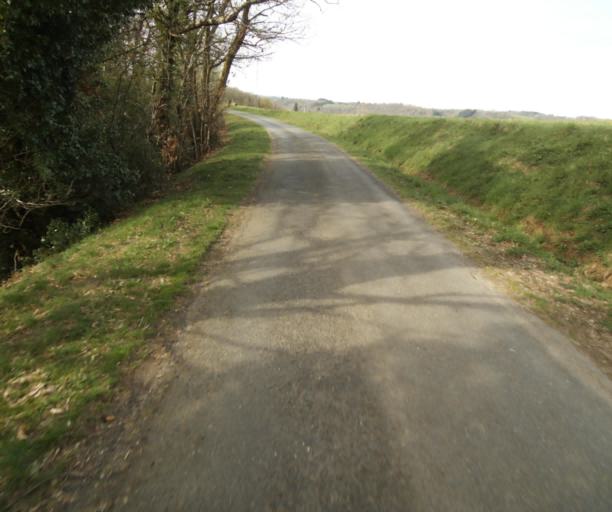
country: FR
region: Limousin
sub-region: Departement de la Correze
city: Correze
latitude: 45.4138
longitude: 1.8076
